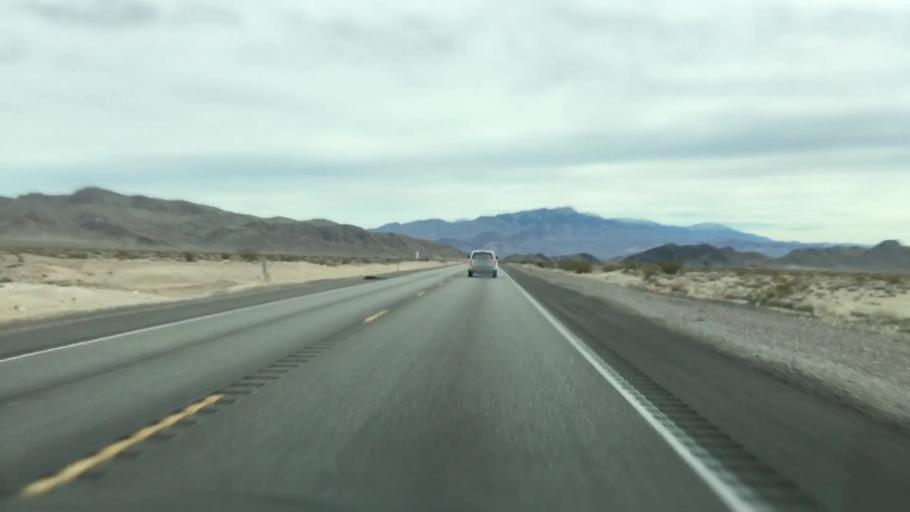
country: US
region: Nevada
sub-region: Nye County
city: Pahrump
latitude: 36.6006
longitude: -116.2475
